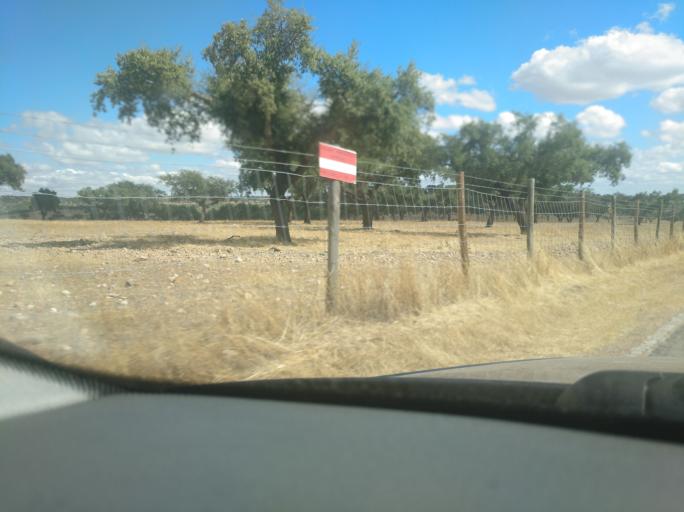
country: ES
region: Extremadura
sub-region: Provincia de Badajoz
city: La Codosera
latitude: 39.1448
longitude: -7.1570
